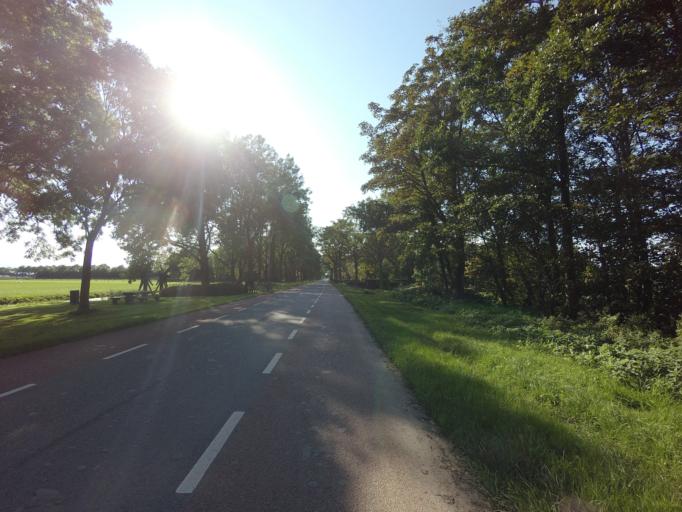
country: NL
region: North Holland
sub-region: Gemeente Enkhuizen
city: Enkhuizen
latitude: 52.6757
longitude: 5.2107
